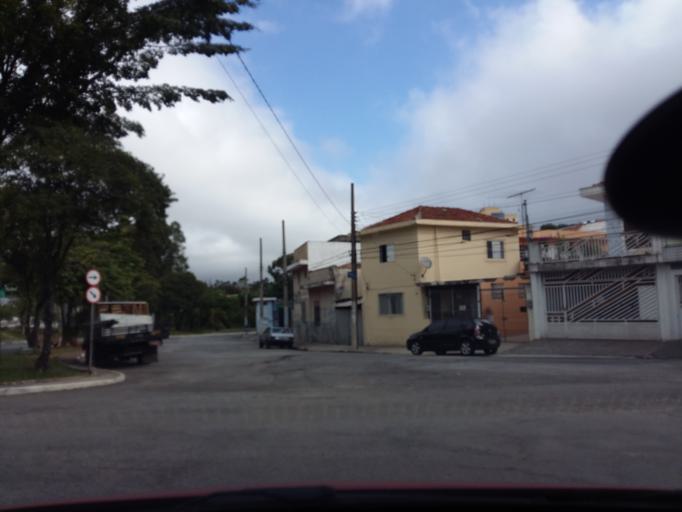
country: BR
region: Sao Paulo
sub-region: Sao Caetano Do Sul
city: Sao Caetano do Sul
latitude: -23.6371
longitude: -46.5952
